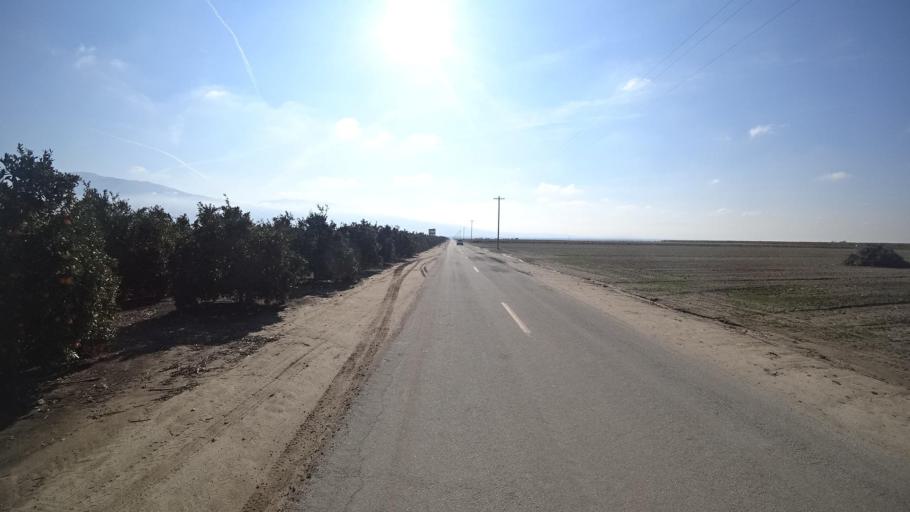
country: US
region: California
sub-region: Kern County
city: Arvin
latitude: 35.2881
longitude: -118.7708
